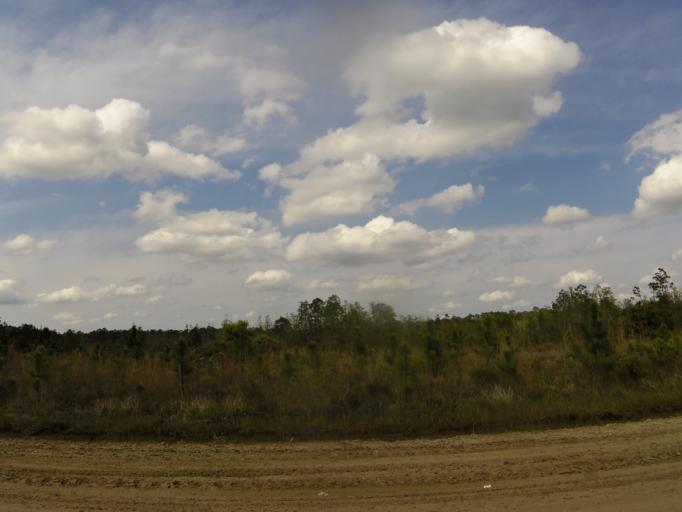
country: US
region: Georgia
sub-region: Charlton County
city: Folkston
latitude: 30.9411
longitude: -82.0171
